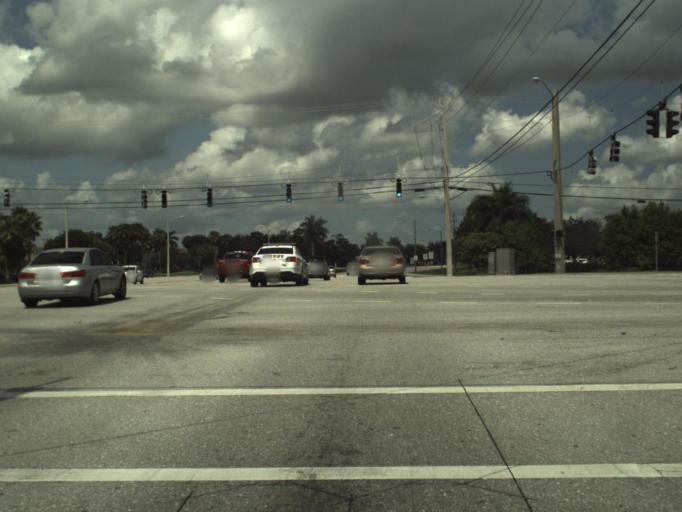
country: US
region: Florida
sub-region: Palm Beach County
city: Wellington
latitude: 26.6509
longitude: -80.2031
